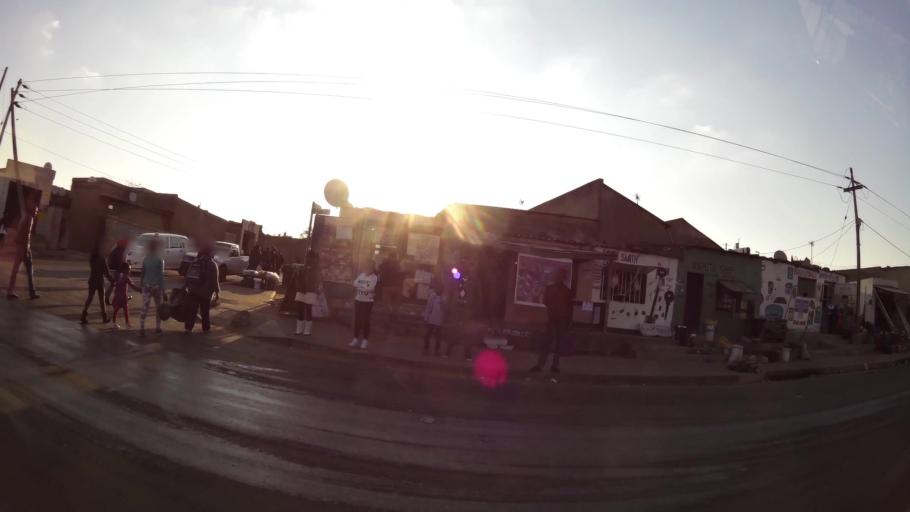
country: ZA
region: Gauteng
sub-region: Ekurhuleni Metropolitan Municipality
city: Tembisa
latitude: -26.0141
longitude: 28.1854
